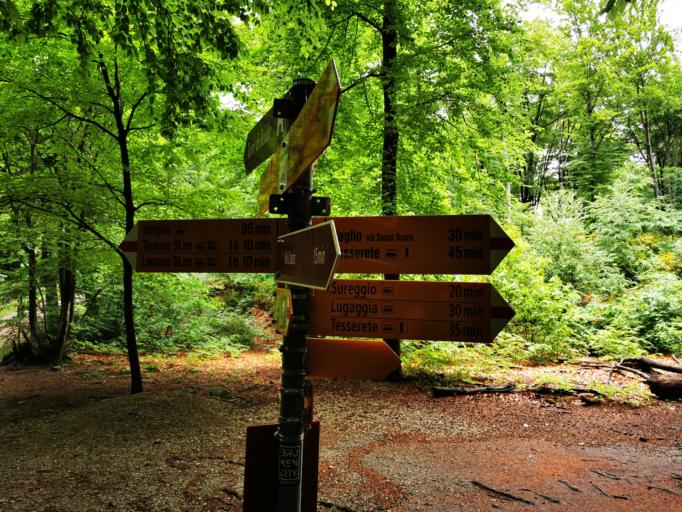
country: CH
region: Ticino
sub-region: Lugano District
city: Canobbio
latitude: 46.0505
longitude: 8.9635
